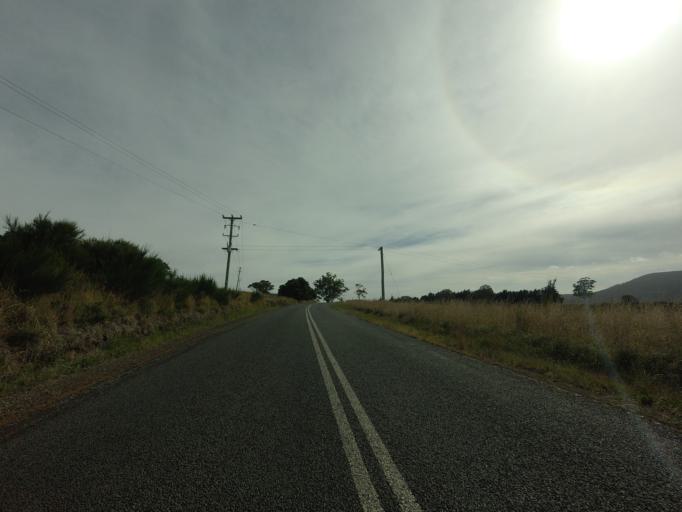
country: AU
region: Tasmania
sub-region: Brighton
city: Bridgewater
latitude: -42.3811
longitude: 147.4245
